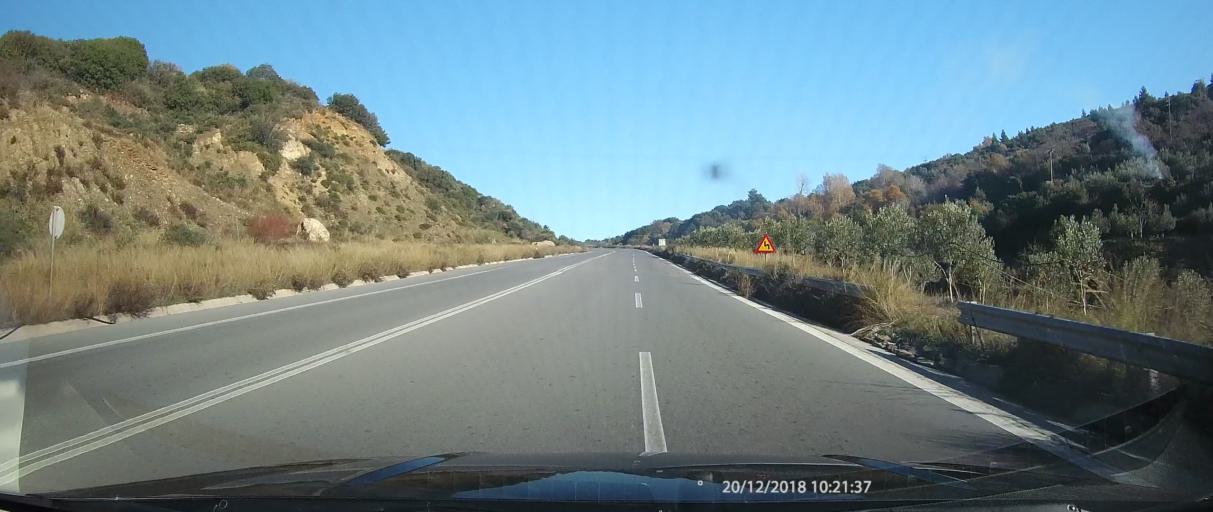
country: GR
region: Peloponnese
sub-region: Nomos Lakonias
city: Magoula
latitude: 37.1627
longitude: 22.4265
